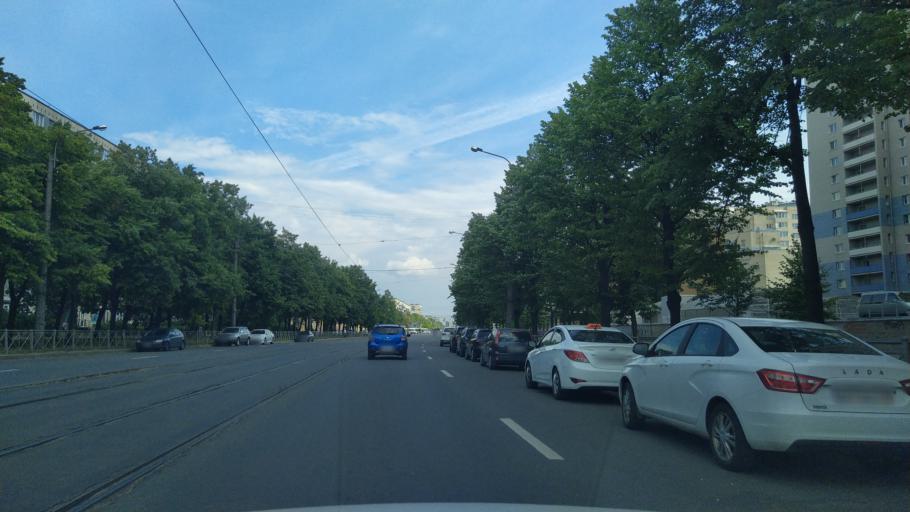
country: RU
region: Leningrad
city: Akademicheskoe
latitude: 60.0144
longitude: 30.3917
